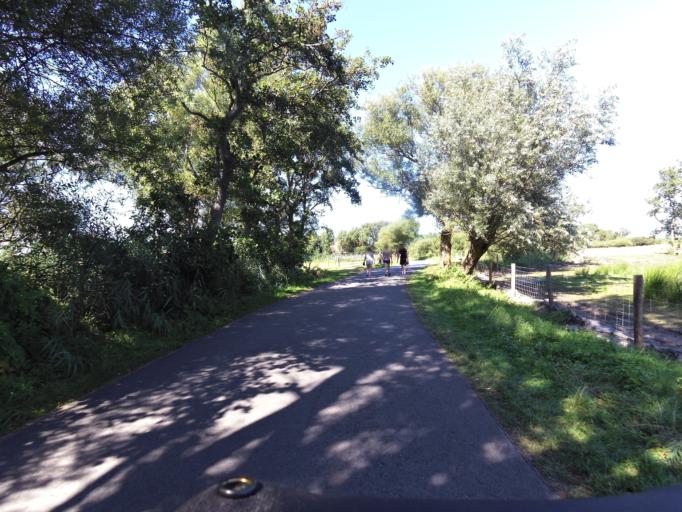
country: NL
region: Zeeland
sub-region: Schouwen-Duiveland
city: Renesse
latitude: 51.7305
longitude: 3.7422
